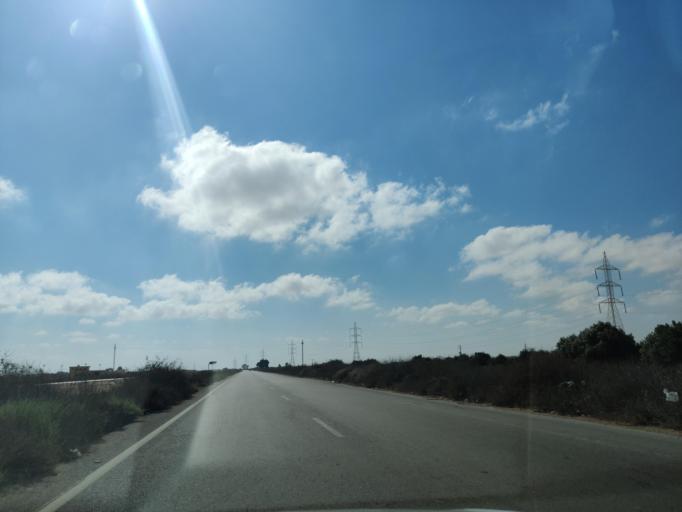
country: EG
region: Muhafazat Matruh
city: Al `Alamayn
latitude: 31.0556
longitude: 28.2564
